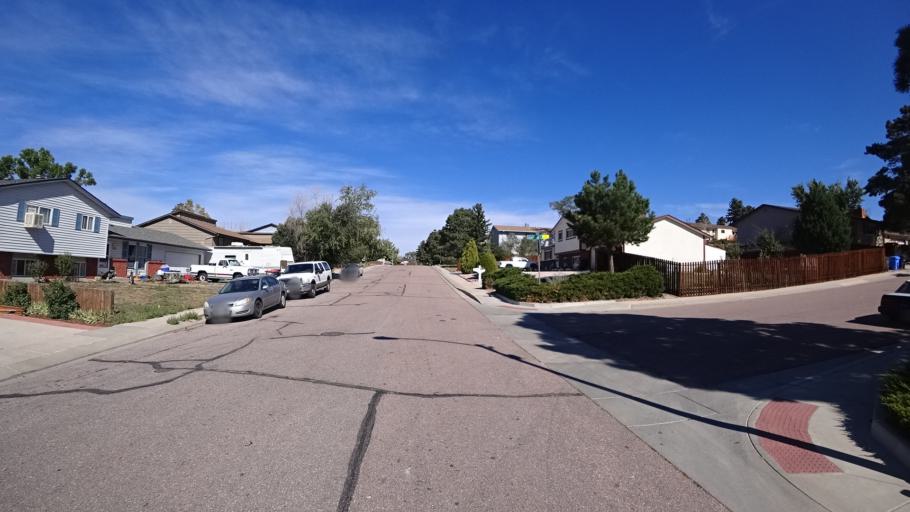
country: US
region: Colorado
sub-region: El Paso County
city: Cimarron Hills
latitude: 38.9160
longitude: -104.7738
